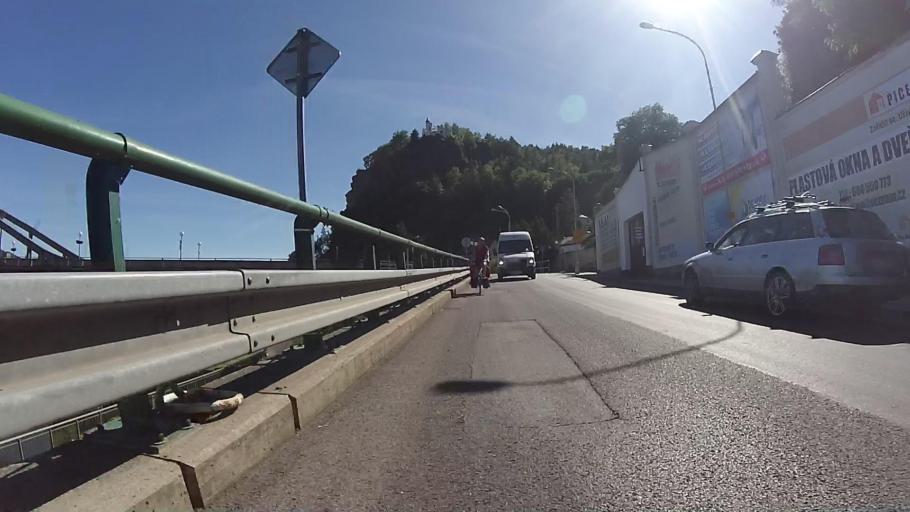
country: CZ
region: Ustecky
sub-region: Okres Decin
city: Decin
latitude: 50.7818
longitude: 14.2068
